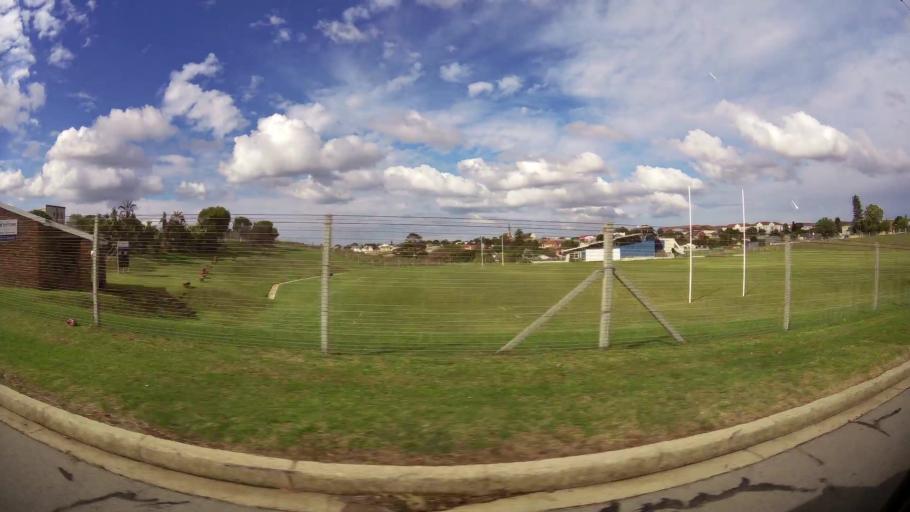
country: ZA
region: Eastern Cape
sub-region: Nelson Mandela Bay Metropolitan Municipality
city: Port Elizabeth
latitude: -33.9432
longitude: 25.5704
